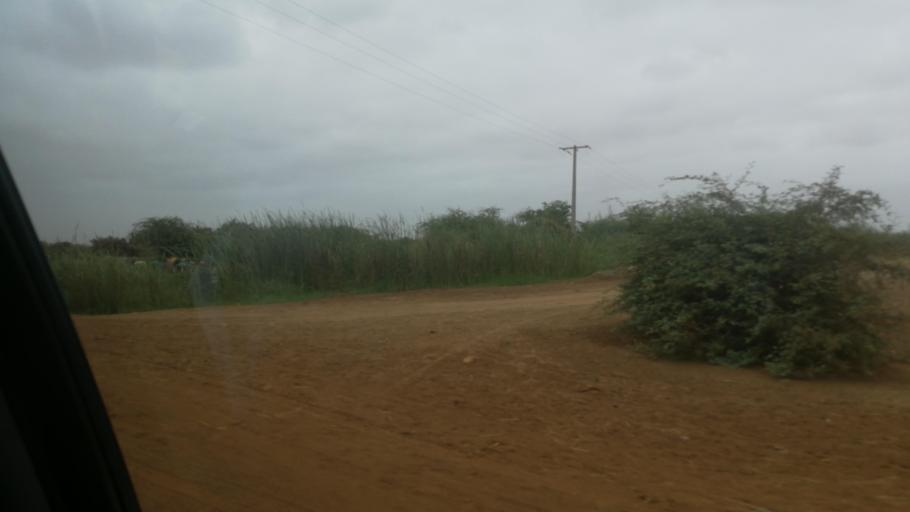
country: SN
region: Saint-Louis
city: Rosso
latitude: 16.2797
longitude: -16.1638
